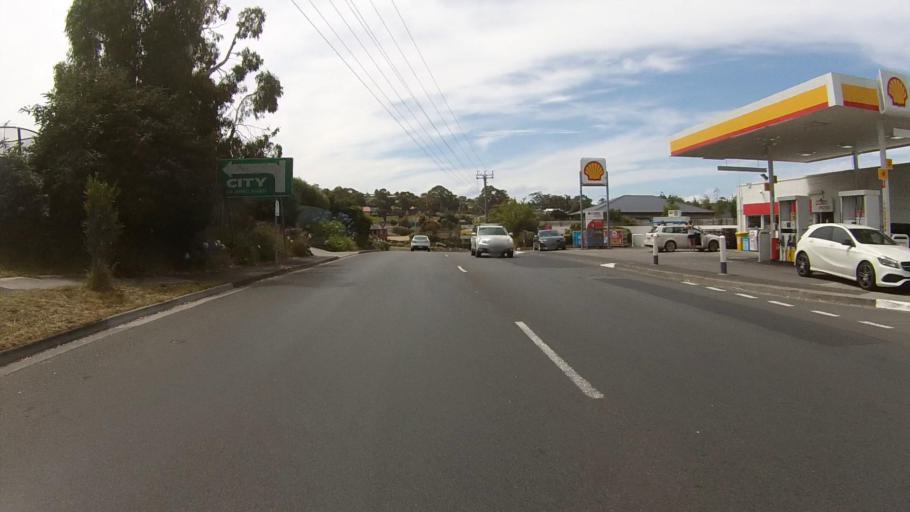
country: AU
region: Tasmania
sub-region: Kingborough
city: Blackmans Bay
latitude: -43.0003
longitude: 147.3203
